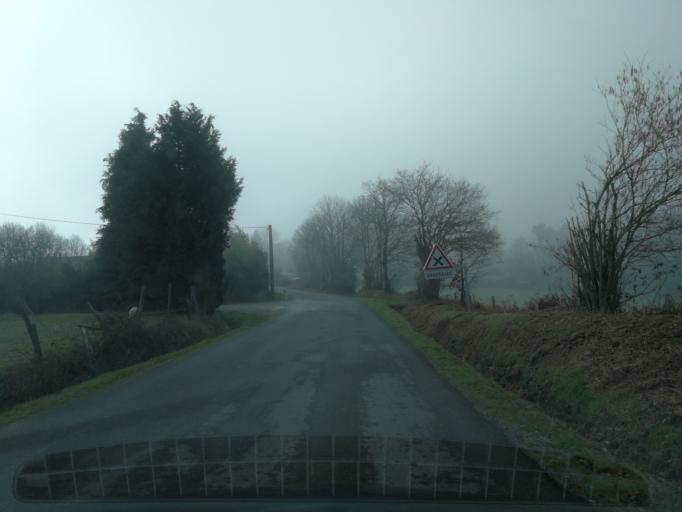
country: FR
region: Brittany
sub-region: Departement du Morbihan
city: La Vraie-Croix
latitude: 47.7211
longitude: -2.5118
